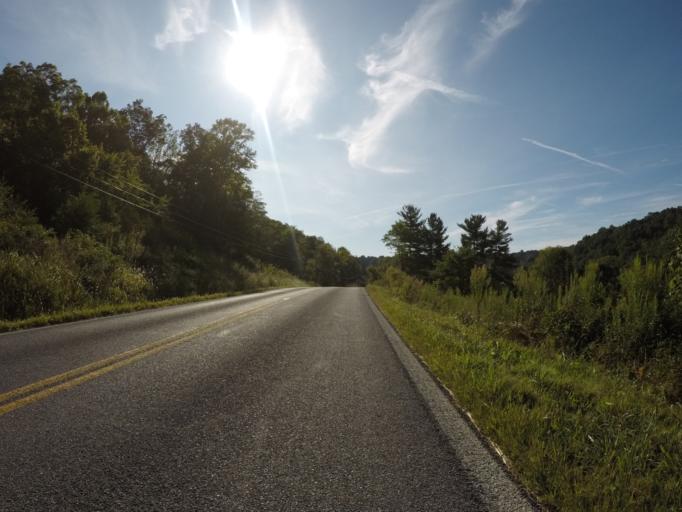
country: US
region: Ohio
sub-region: Lawrence County
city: Burlington
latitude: 38.4970
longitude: -82.5026
